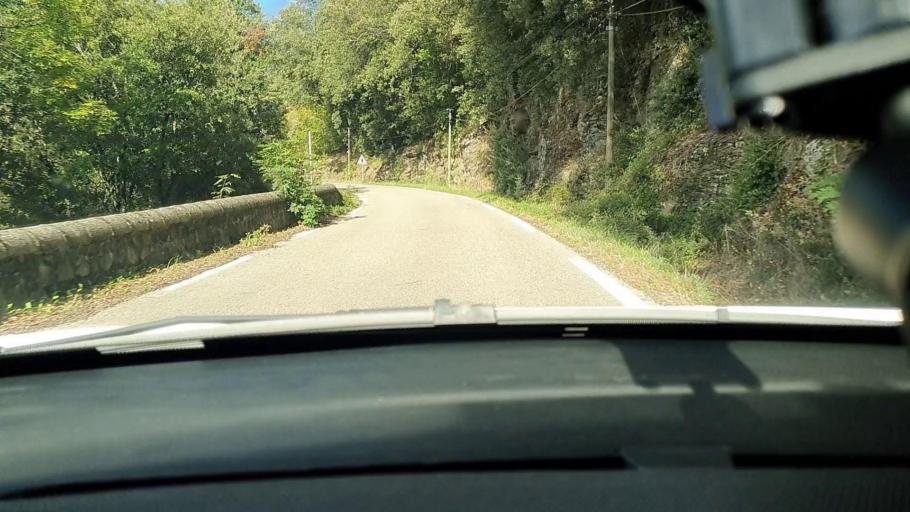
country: FR
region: Languedoc-Roussillon
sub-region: Departement du Gard
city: Besseges
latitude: 44.3833
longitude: 3.9834
